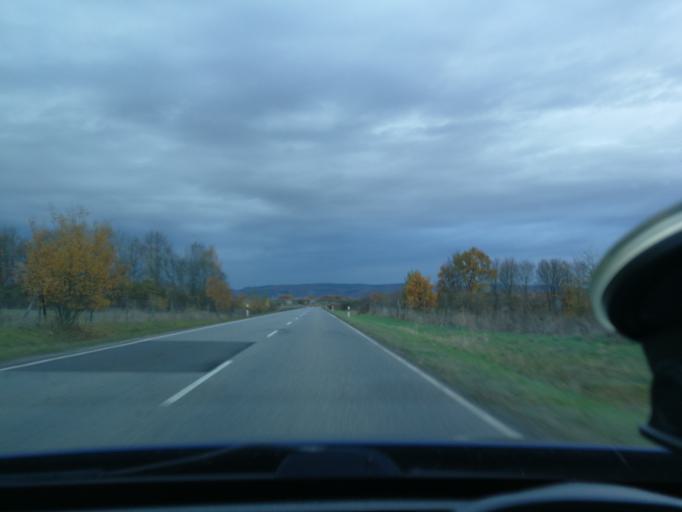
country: DE
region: Rheinland-Pfalz
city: Altrich
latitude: 49.9394
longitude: 6.9312
